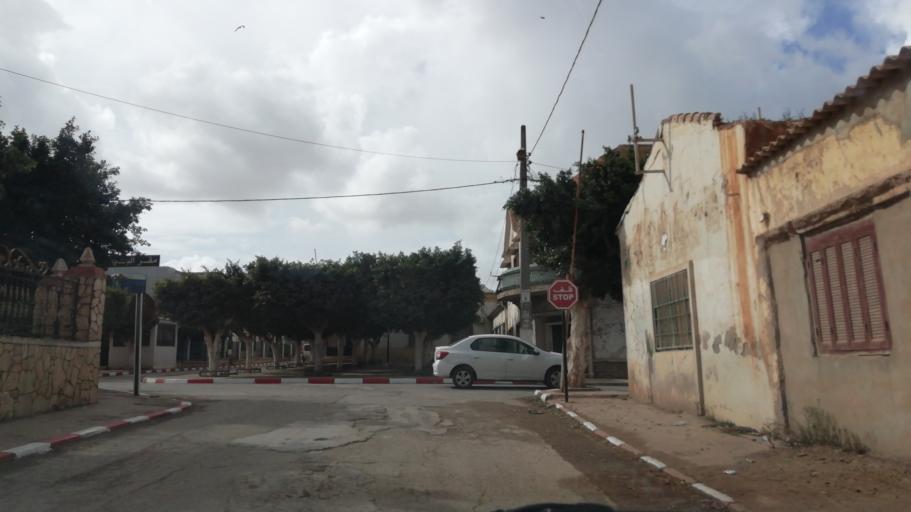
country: DZ
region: Oran
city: Es Senia
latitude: 35.6124
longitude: -0.5792
